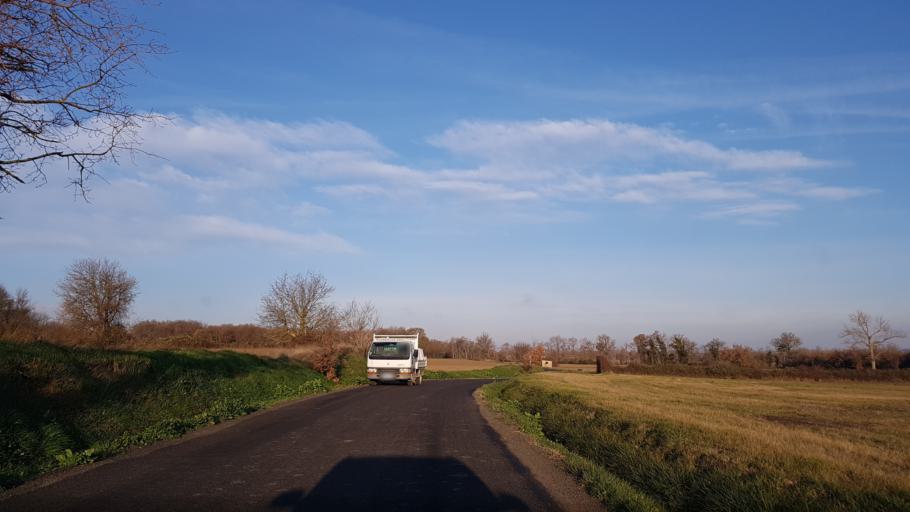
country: FR
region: Languedoc-Roussillon
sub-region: Departement de l'Aude
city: Villeneuve-la-Comptal
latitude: 43.2812
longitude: 1.9377
